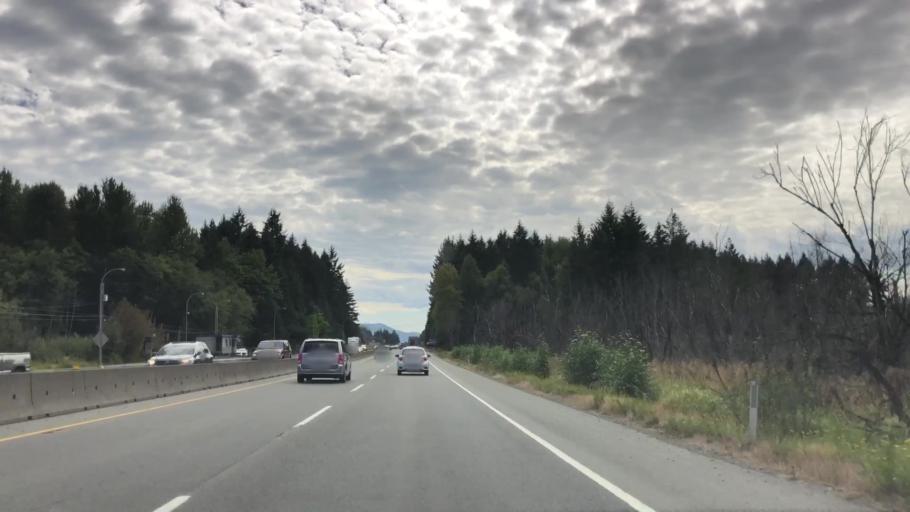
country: CA
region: British Columbia
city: North Cowichan
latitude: 48.8322
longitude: -123.7182
